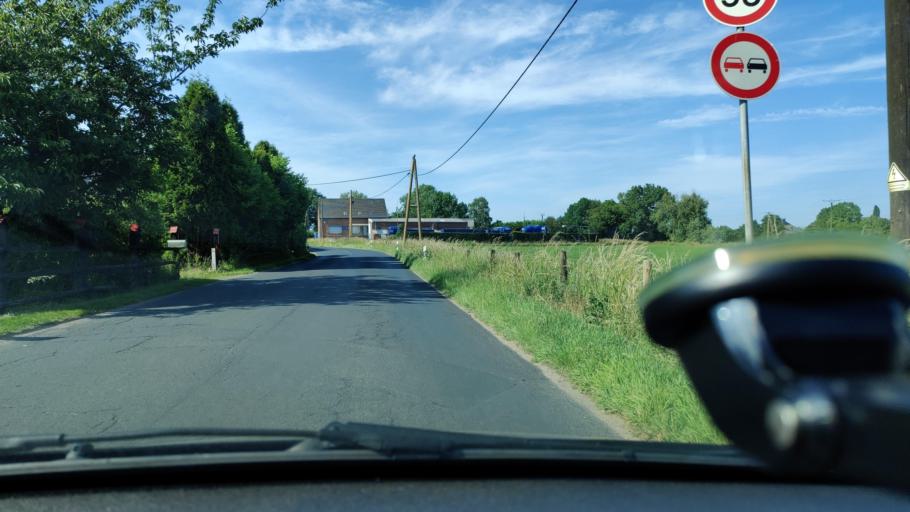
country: DE
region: North Rhine-Westphalia
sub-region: Regierungsbezirk Dusseldorf
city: Kamp-Lintfort
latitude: 51.5173
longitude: 6.5154
